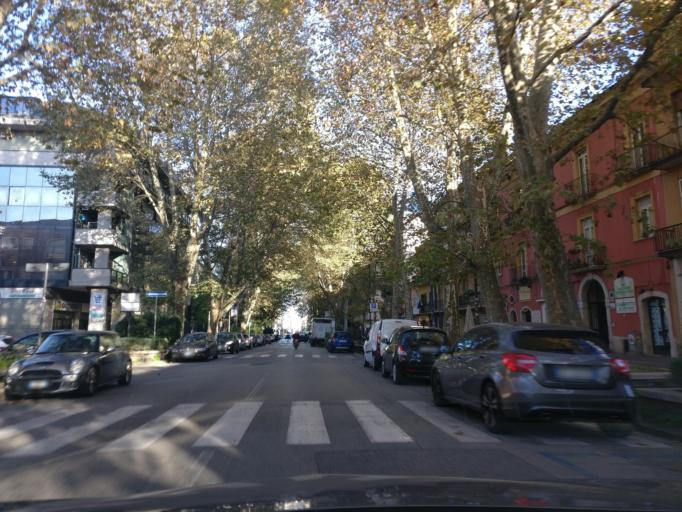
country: IT
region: Campania
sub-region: Provincia di Avellino
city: Avellino
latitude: 40.9130
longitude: 14.7812
